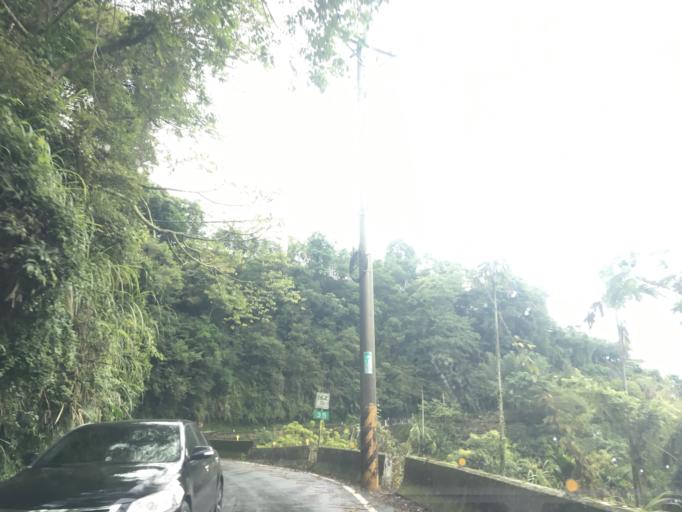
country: TW
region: Taiwan
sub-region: Yunlin
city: Douliu
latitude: 23.5598
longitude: 120.6623
